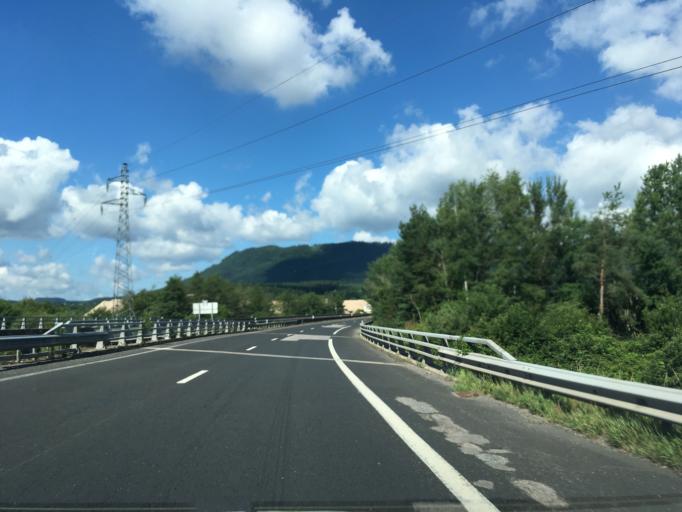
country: FR
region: Lorraine
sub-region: Departement des Vosges
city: Sainte-Marguerite
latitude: 48.2616
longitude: 6.9749
